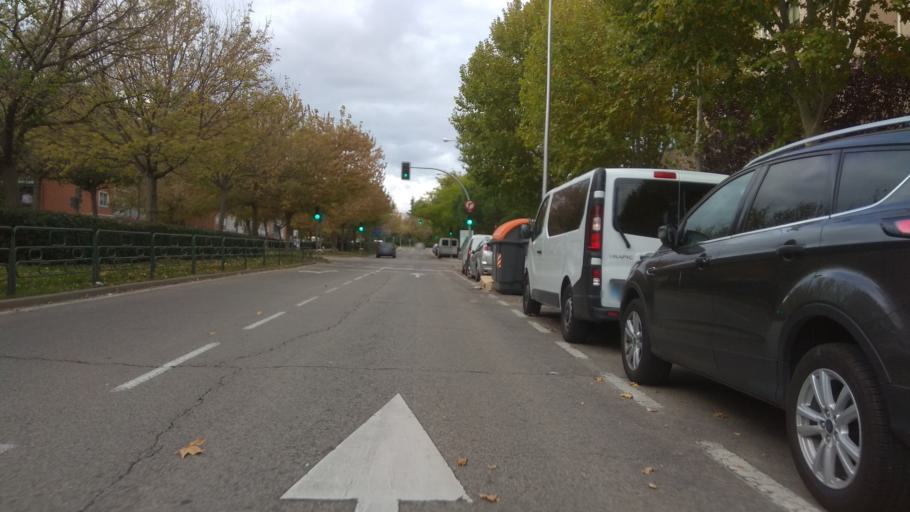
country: ES
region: Madrid
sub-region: Provincia de Madrid
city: Vicalvaro
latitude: 40.4088
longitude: -3.6075
